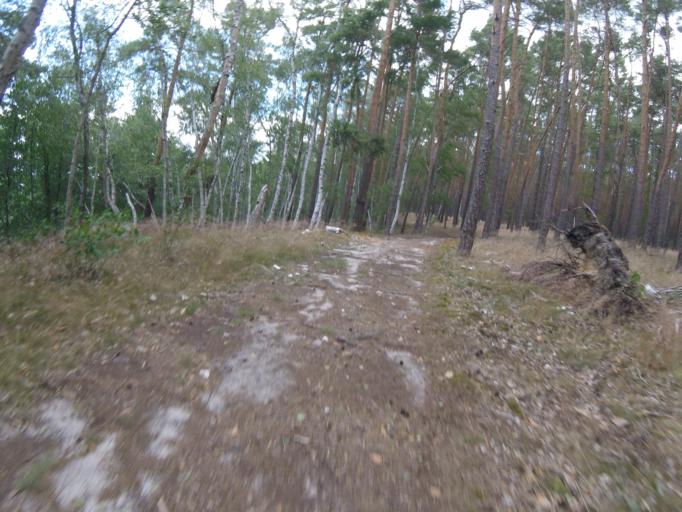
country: DE
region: Brandenburg
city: Gross Koris
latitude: 52.2026
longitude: 13.6390
